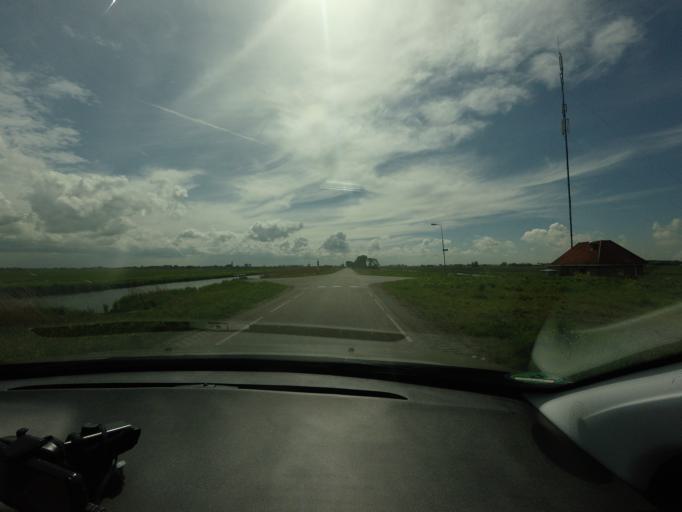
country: NL
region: North Holland
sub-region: Gemeente Heerhugowaard
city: Heerhugowaard
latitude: 52.6167
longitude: 4.8851
